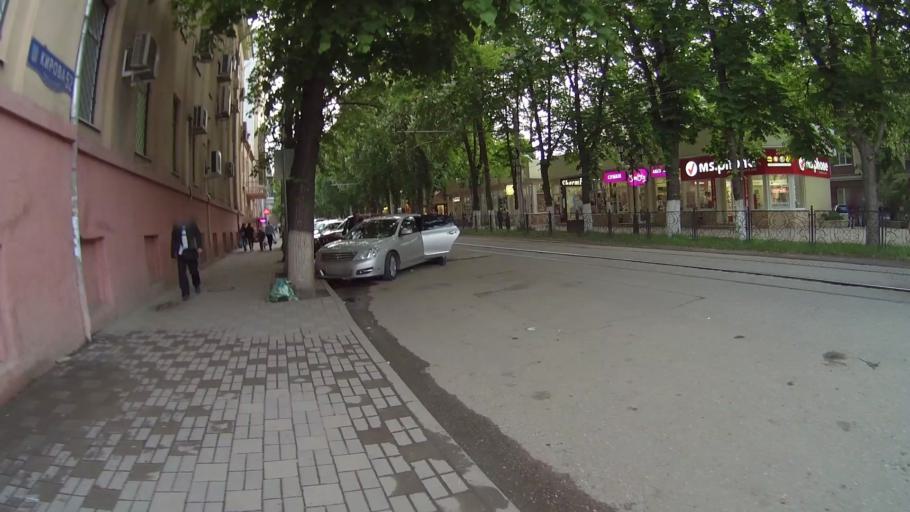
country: RU
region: Stavropol'skiy
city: Pyatigorsk
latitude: 44.0363
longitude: 43.0715
